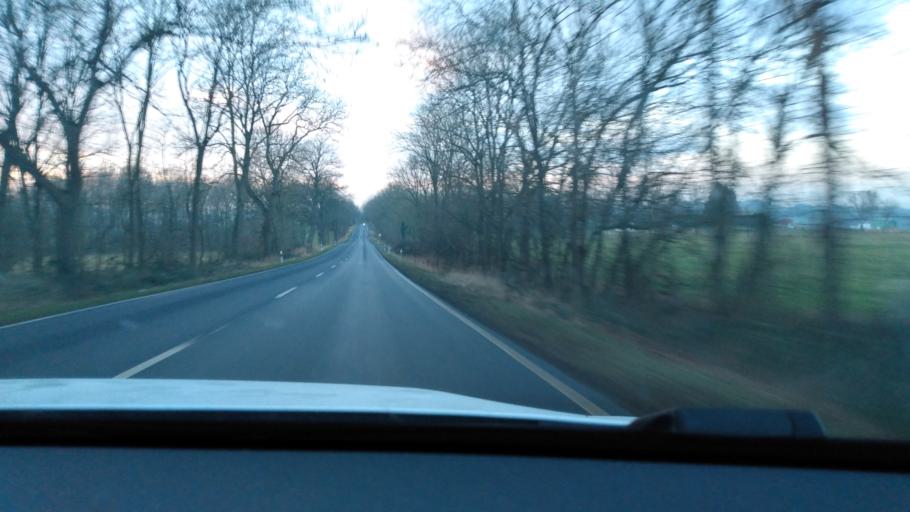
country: DE
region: Rheinland-Pfalz
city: Asbach
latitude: 50.7186
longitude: 7.3904
